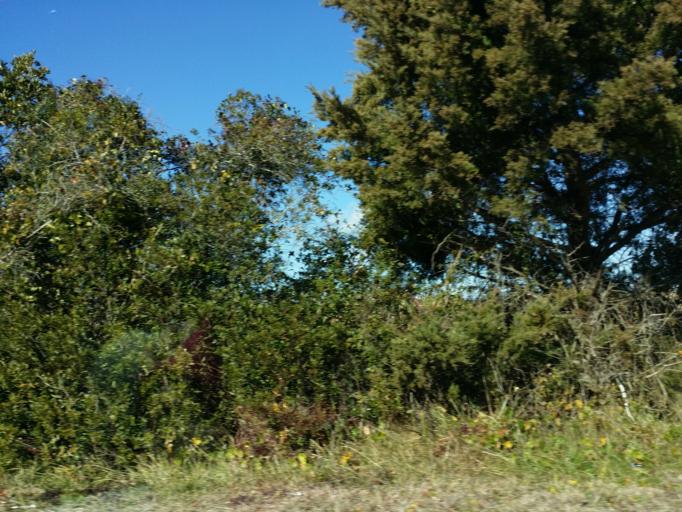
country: US
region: North Carolina
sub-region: Pender County
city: Surf City
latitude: 34.4378
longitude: -77.5280
